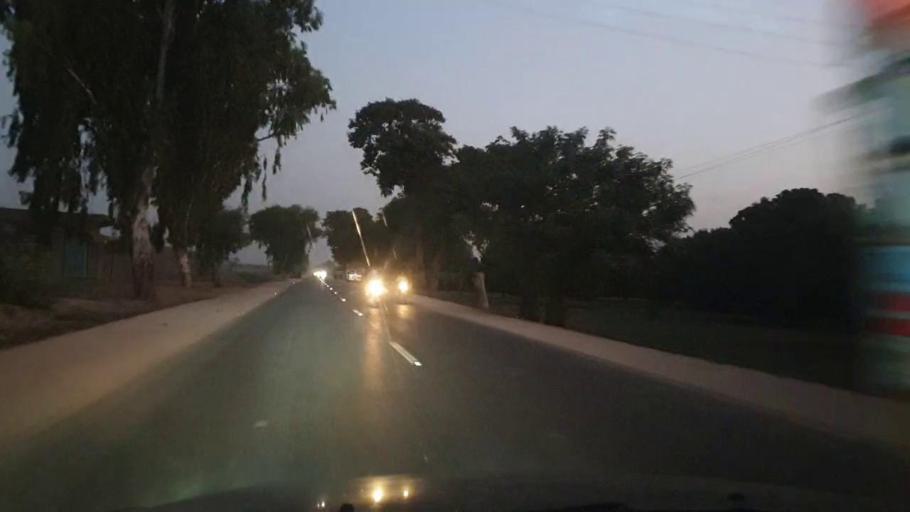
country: PK
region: Sindh
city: Tando Allahyar
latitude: 25.4040
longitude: 68.7607
